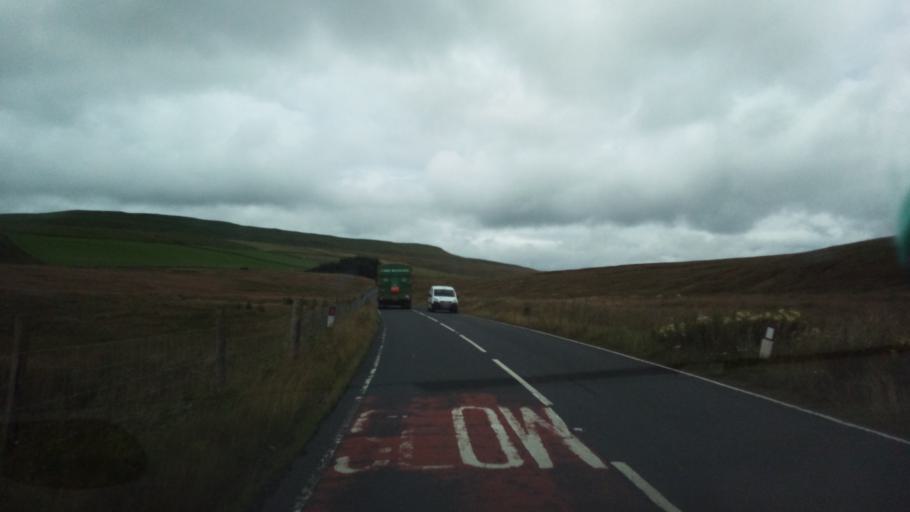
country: GB
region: England
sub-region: North Yorkshire
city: Ingleton
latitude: 54.2464
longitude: -2.3160
